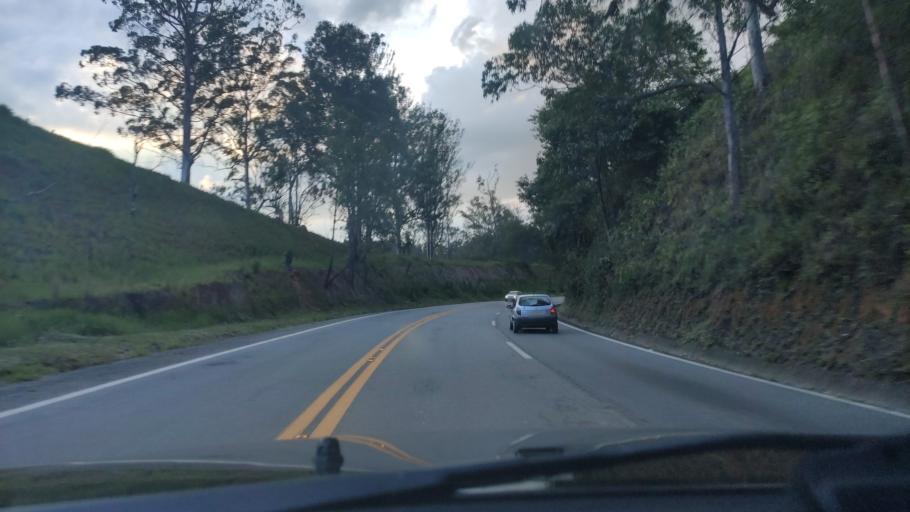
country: BR
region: Sao Paulo
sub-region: Braganca Paulista
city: Braganca Paulista
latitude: -22.8369
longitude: -46.5557
